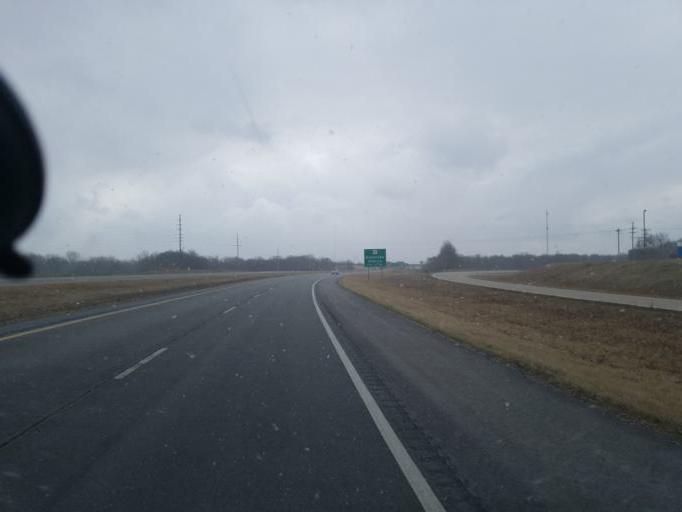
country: US
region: Missouri
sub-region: Randolph County
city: Moberly
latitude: 39.4255
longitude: -92.4123
